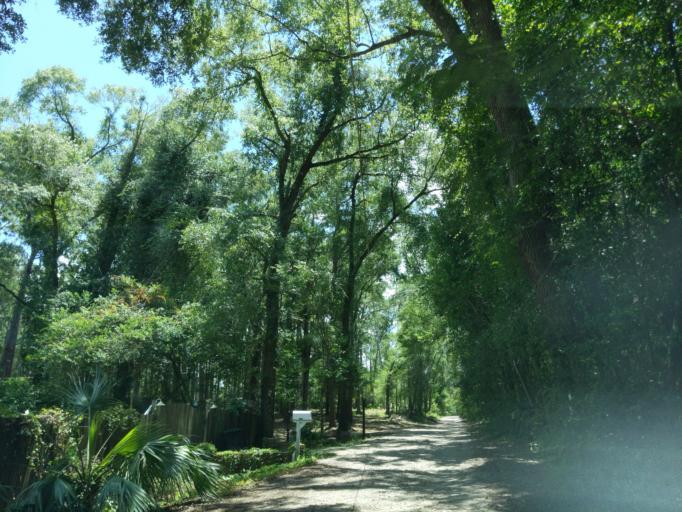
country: US
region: Florida
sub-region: Leon County
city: Tallahassee
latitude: 30.4051
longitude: -84.3445
